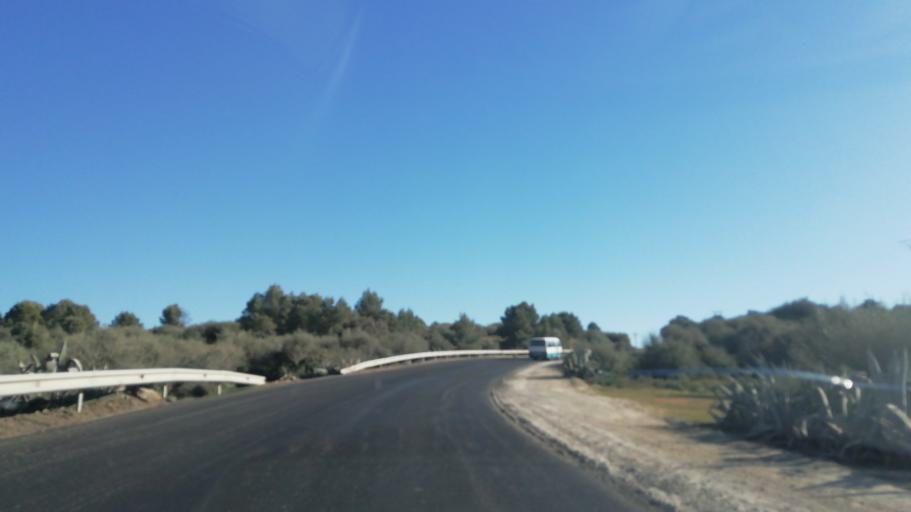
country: DZ
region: Relizane
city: Smala
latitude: 35.6670
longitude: 0.8103
